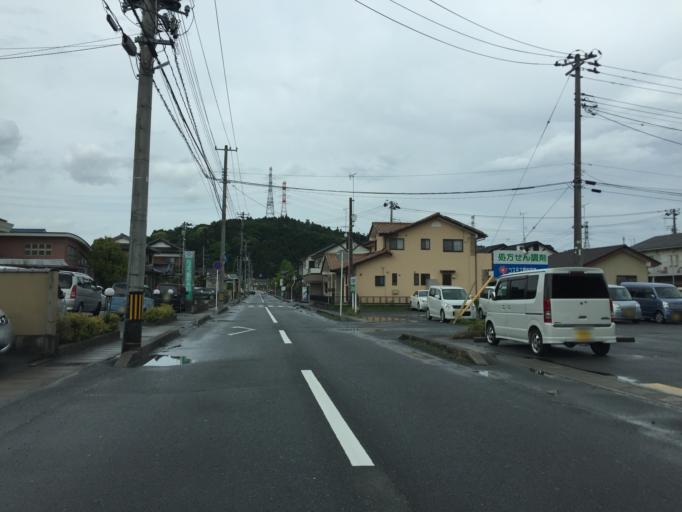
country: JP
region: Ibaraki
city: Kitaibaraki
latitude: 36.9189
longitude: 140.8044
